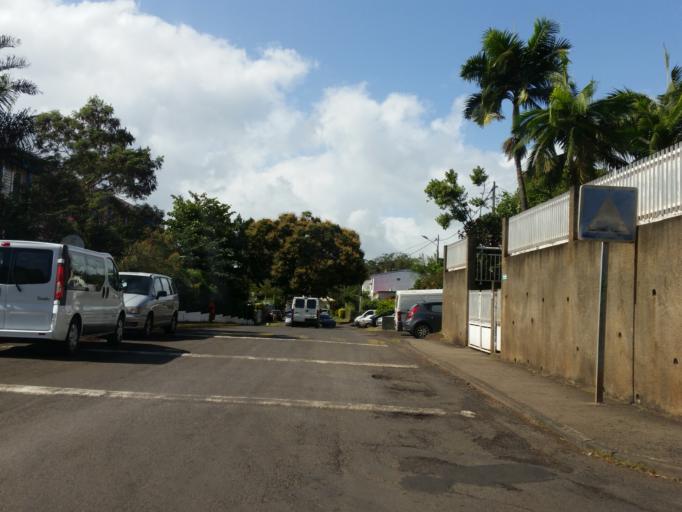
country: RE
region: Reunion
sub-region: Reunion
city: Saint-Denis
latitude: -20.8936
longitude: 55.4646
